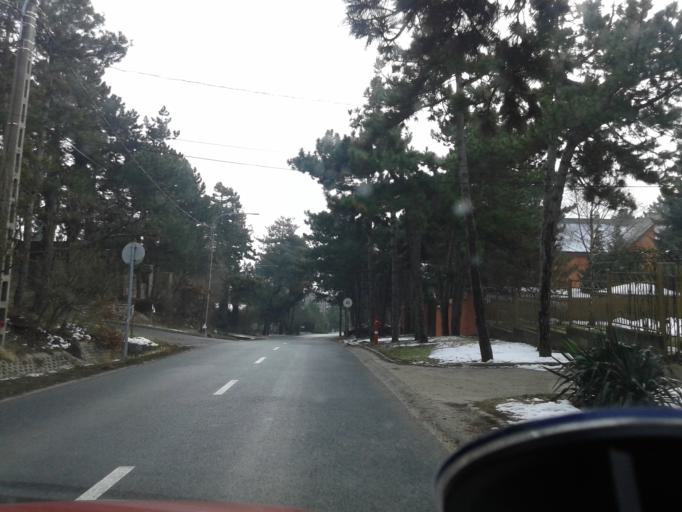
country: HU
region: Pest
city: Diosd
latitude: 47.4088
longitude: 18.9292
